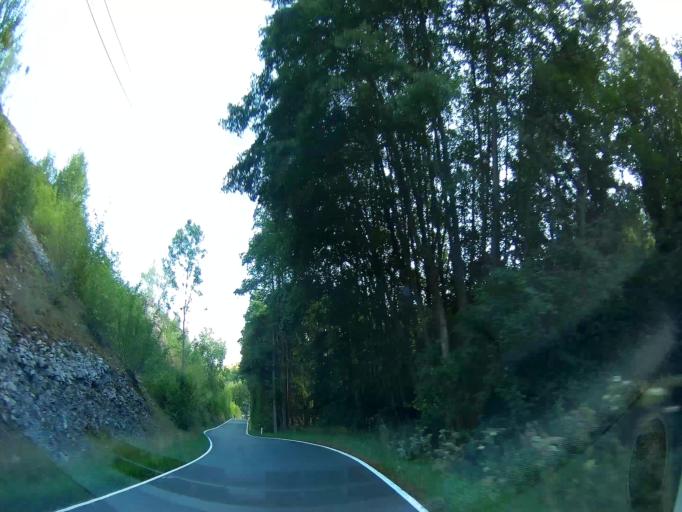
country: BE
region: Wallonia
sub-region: Province de Namur
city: Onhaye
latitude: 50.2980
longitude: 4.7771
